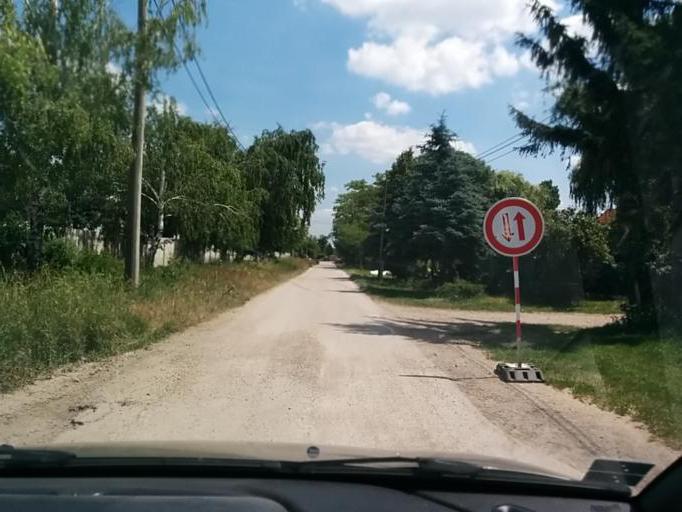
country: SK
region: Trnavsky
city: Sladkovicovo
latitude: 48.2019
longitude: 17.5250
